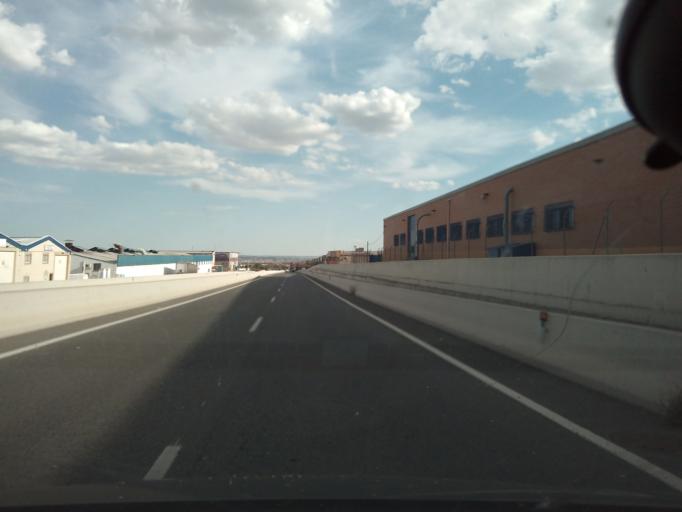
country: ES
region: Madrid
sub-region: Provincia de Madrid
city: Ajalvir
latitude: 40.5115
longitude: -3.4805
